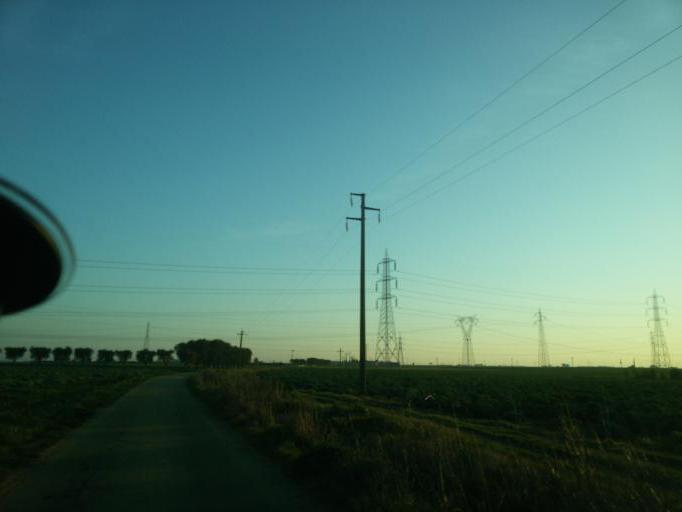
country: IT
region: Apulia
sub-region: Provincia di Brindisi
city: La Rosa
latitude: 40.6016
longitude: 17.9396
